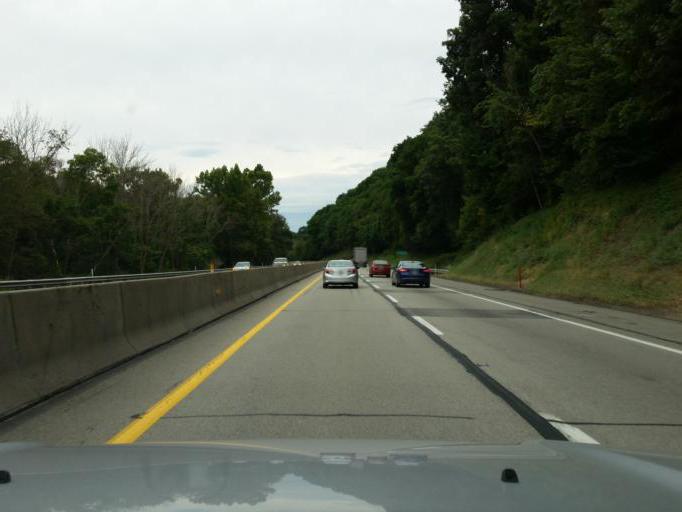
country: US
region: Pennsylvania
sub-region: Westmoreland County
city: Level Green
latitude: 40.4254
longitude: -79.7380
